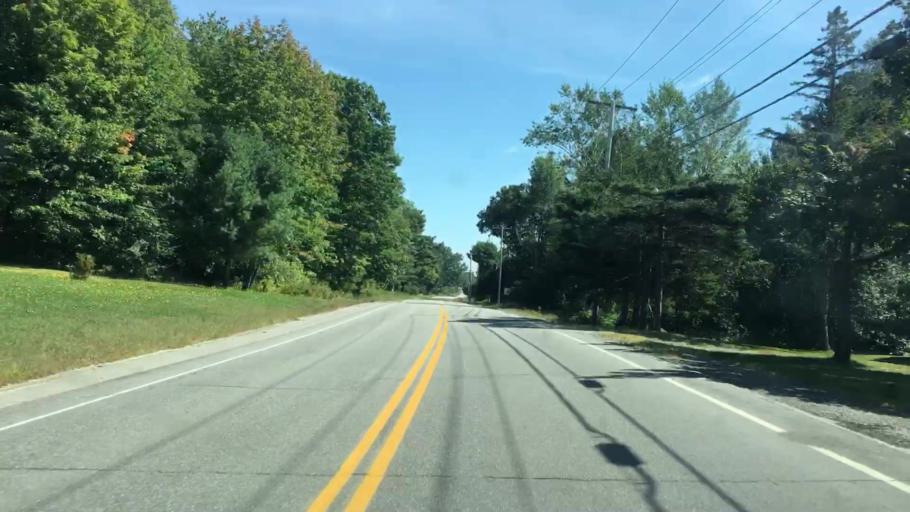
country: US
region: Maine
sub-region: Piscataquis County
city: Milo
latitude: 45.1885
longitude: -68.8950
